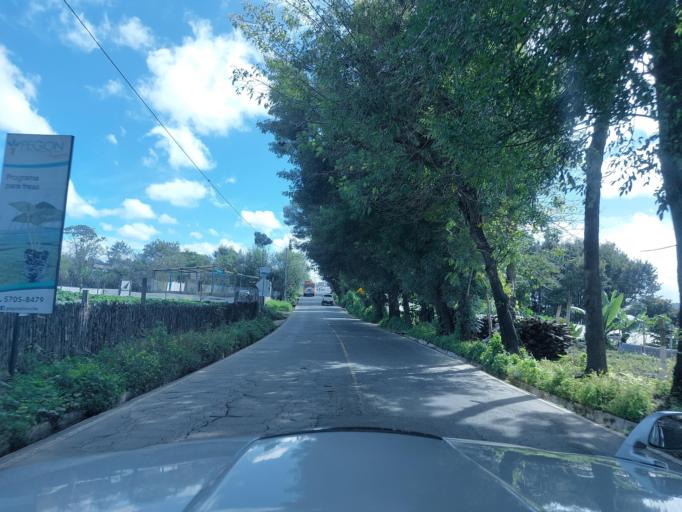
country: GT
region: Chimaltenango
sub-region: Municipio de Zaragoza
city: Zaragoza
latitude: 14.6714
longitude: -90.8992
